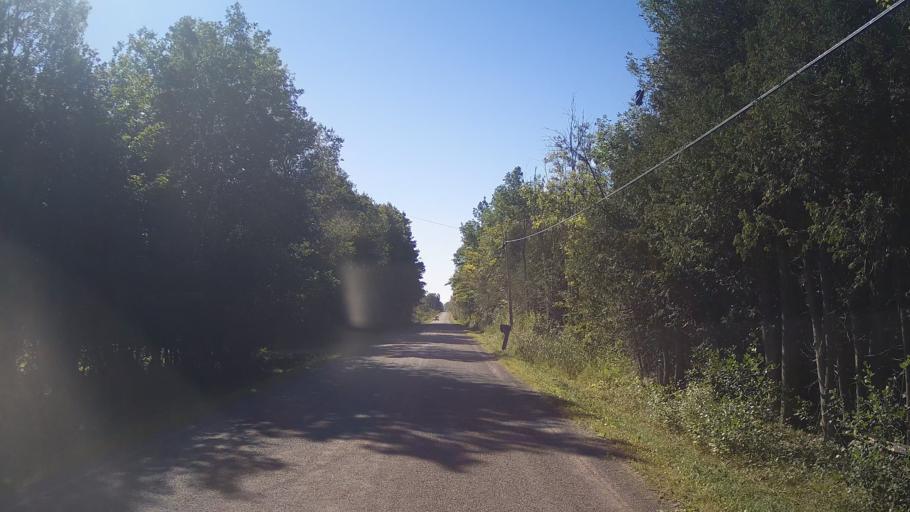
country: CA
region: Ontario
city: Prescott
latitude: 44.9958
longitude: -75.5934
